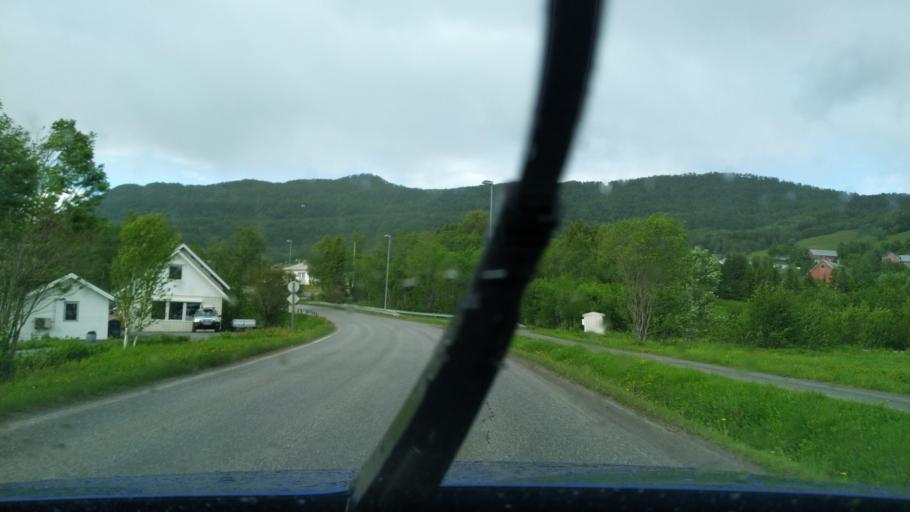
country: NO
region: Troms
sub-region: Sorreisa
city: Sorreisa
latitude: 69.1502
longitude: 18.1705
